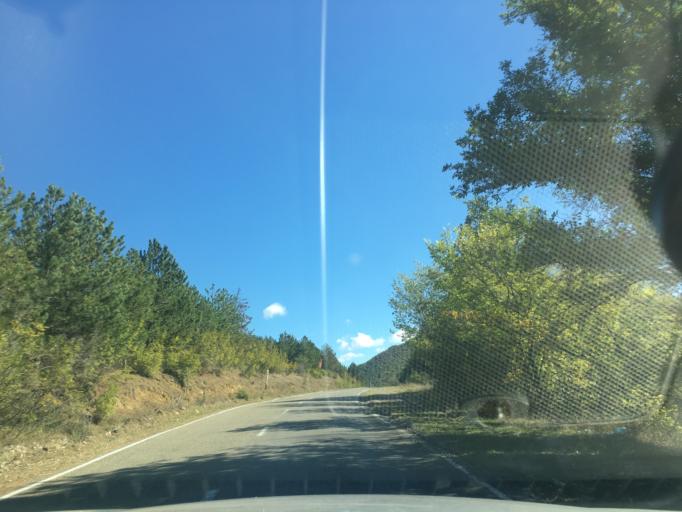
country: GE
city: Zahesi
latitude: 41.8301
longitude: 44.8542
